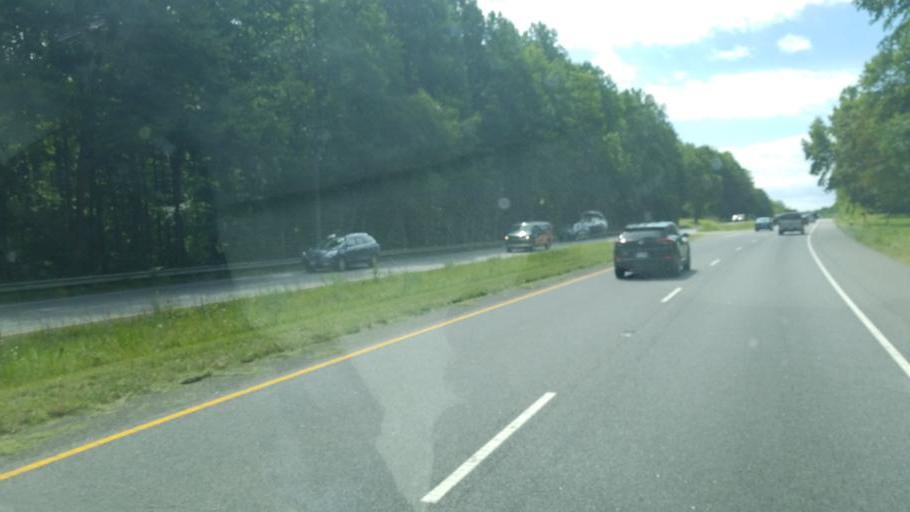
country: US
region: Virginia
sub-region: Stafford County
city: Falmouth
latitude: 38.4248
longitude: -77.6184
